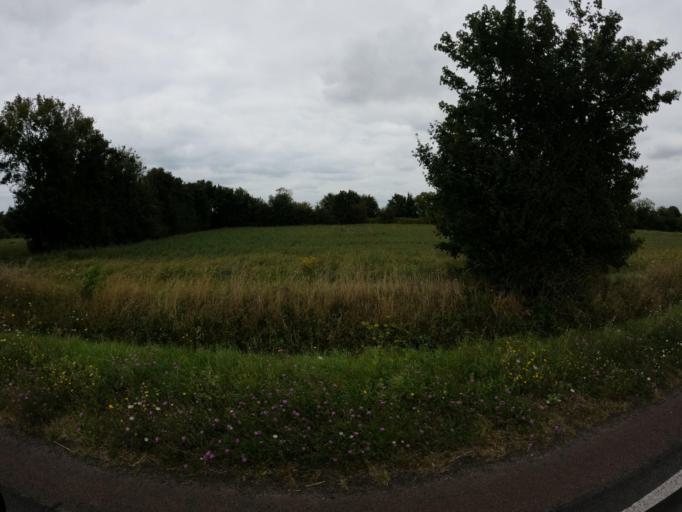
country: FR
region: Pays de la Loire
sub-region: Departement de la Vendee
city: Saint-Michel-le-Cloucq
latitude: 46.4362
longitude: -0.7406
